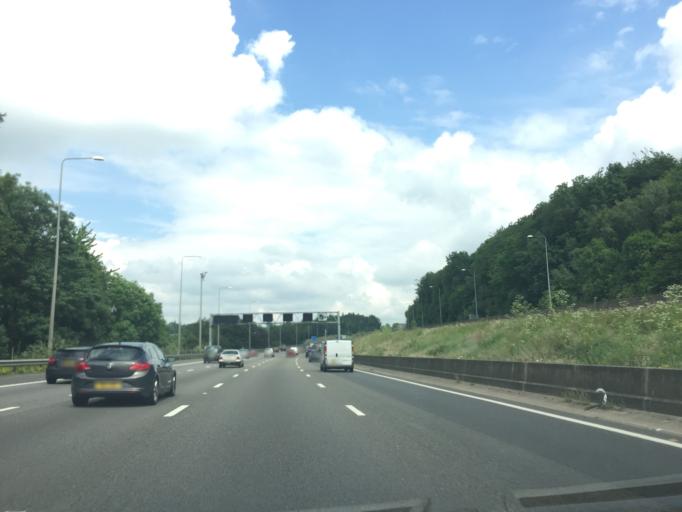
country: GB
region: England
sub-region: Hertfordshire
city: Abbots Langley
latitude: 51.7104
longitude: -0.4297
